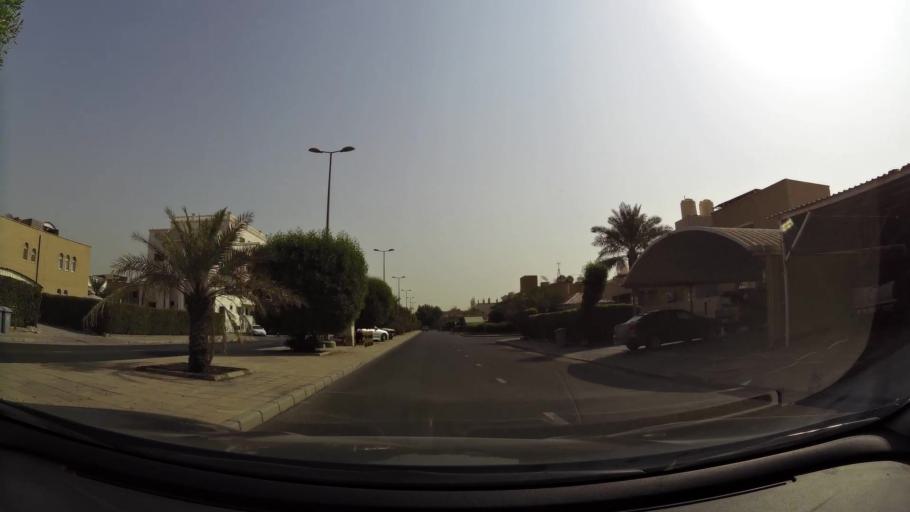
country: KW
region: Al Asimah
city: Ar Rabiyah
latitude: 29.2916
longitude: 47.8912
